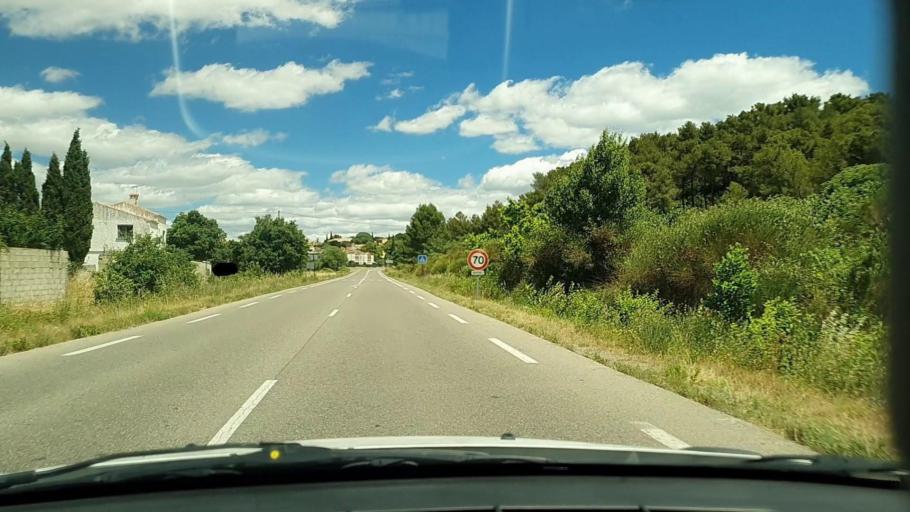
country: FR
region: Languedoc-Roussillon
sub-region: Departement du Gard
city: Marguerittes
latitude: 43.8651
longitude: 4.4041
